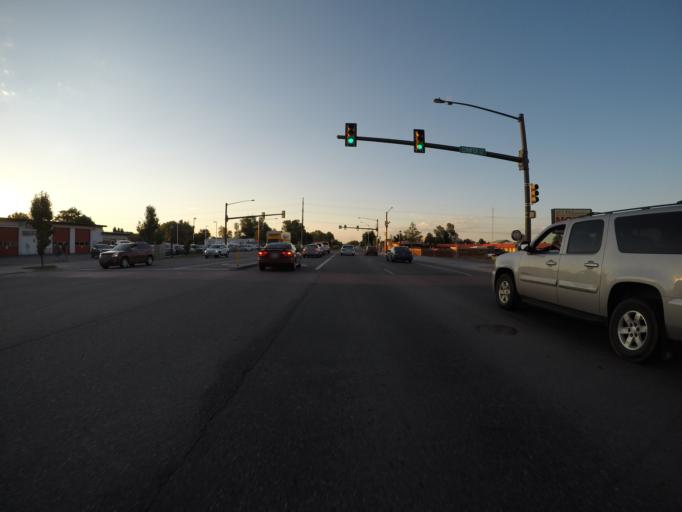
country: US
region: Colorado
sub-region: Larimer County
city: Fort Collins
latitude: 40.6029
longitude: -105.0766
